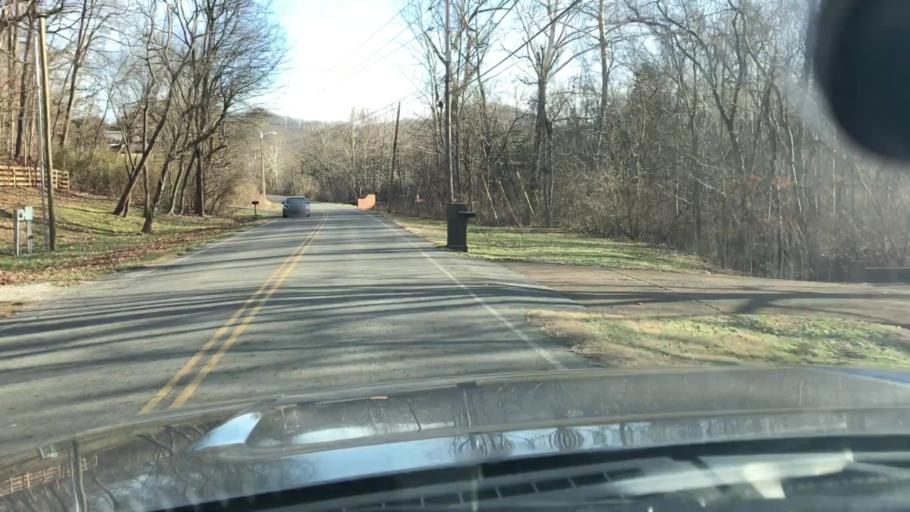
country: US
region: Tennessee
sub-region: Davidson County
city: Forest Hills
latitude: 36.0053
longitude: -86.8426
